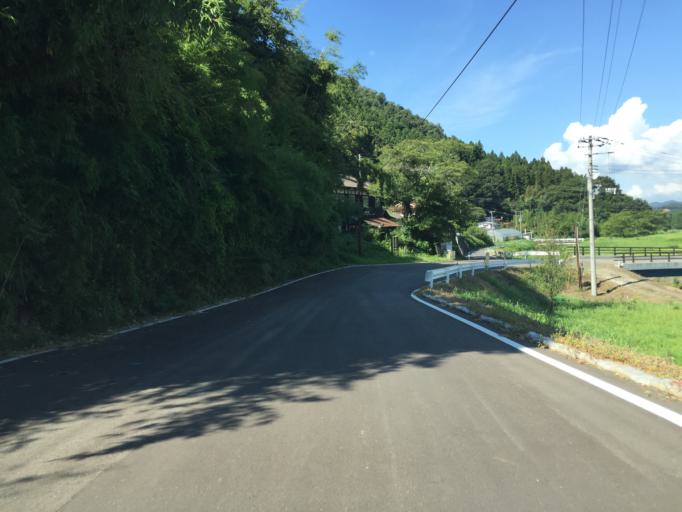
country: JP
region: Fukushima
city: Hobaramachi
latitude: 37.7488
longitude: 140.5638
